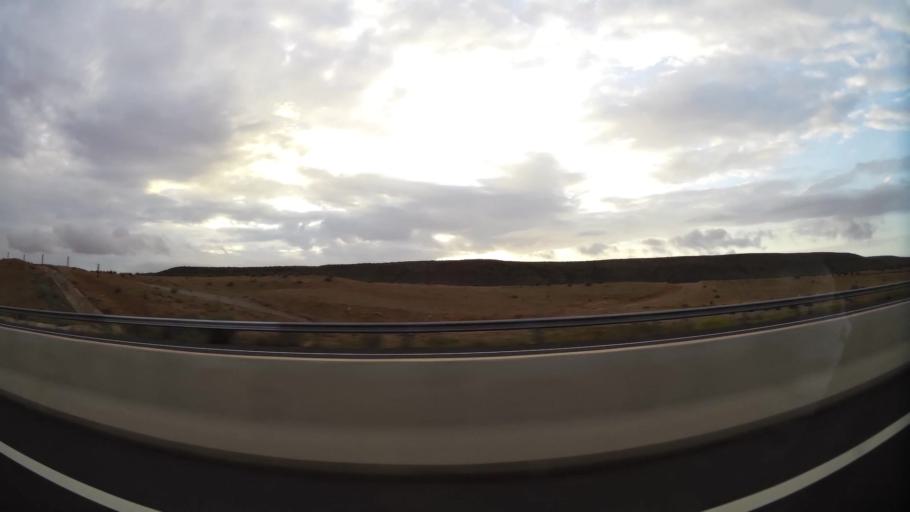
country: MA
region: Oriental
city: Taourirt
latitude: 34.4528
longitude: -3.0483
